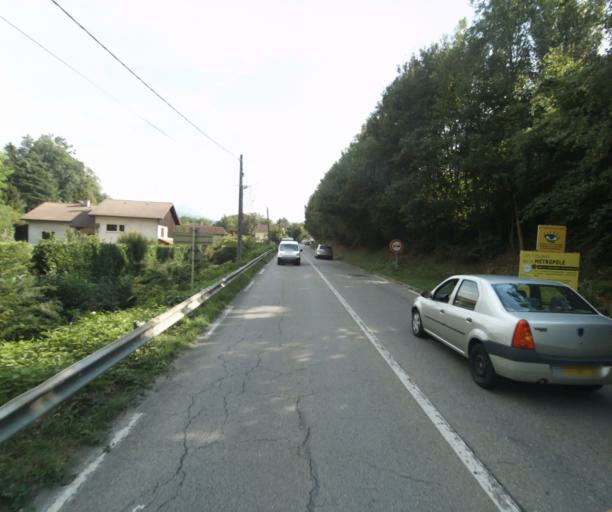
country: FR
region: Rhone-Alpes
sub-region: Departement de l'Isere
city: Poisat
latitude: 45.1413
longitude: 5.7698
